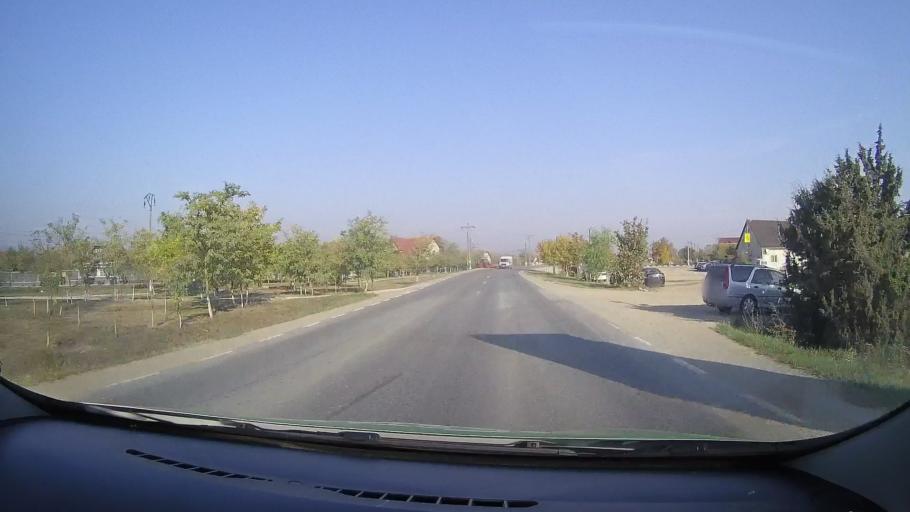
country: RO
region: Arad
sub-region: Comuna Pilu
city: Pilu
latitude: 46.5700
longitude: 21.3426
